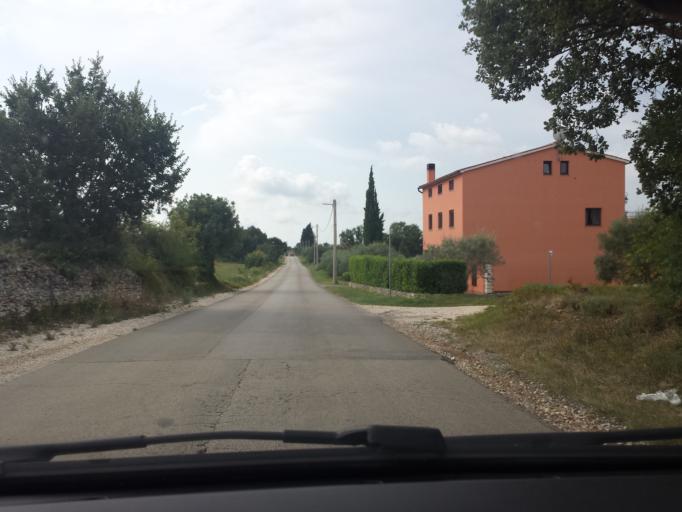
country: HR
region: Istarska
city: Galizana
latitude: 44.9403
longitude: 13.8673
